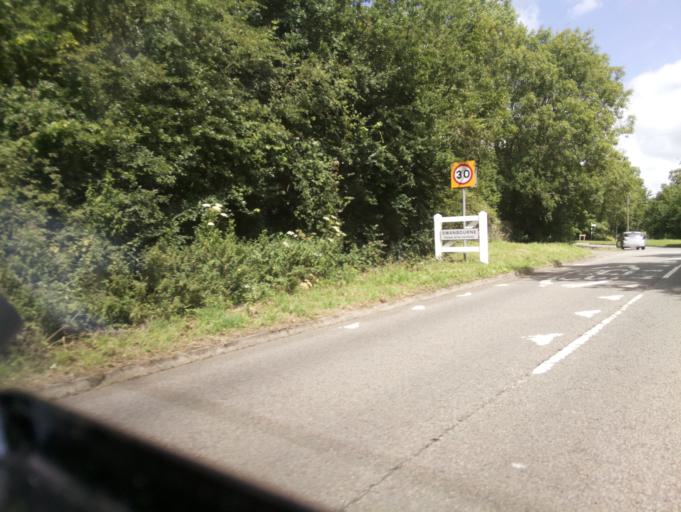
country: GB
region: England
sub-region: Buckinghamshire
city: Winslow
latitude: 51.9341
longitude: -0.8347
